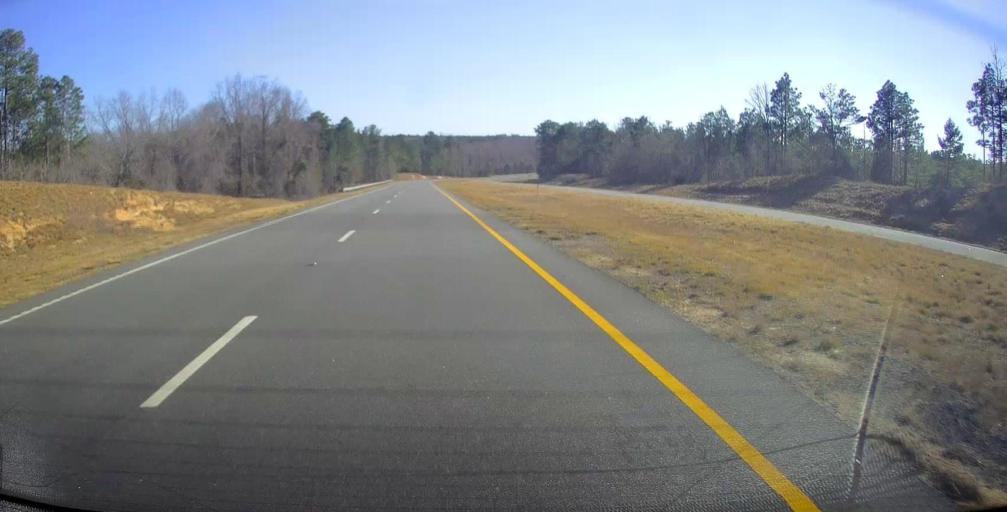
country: US
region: Georgia
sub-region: Taylor County
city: Butler
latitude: 32.5902
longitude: -84.2365
